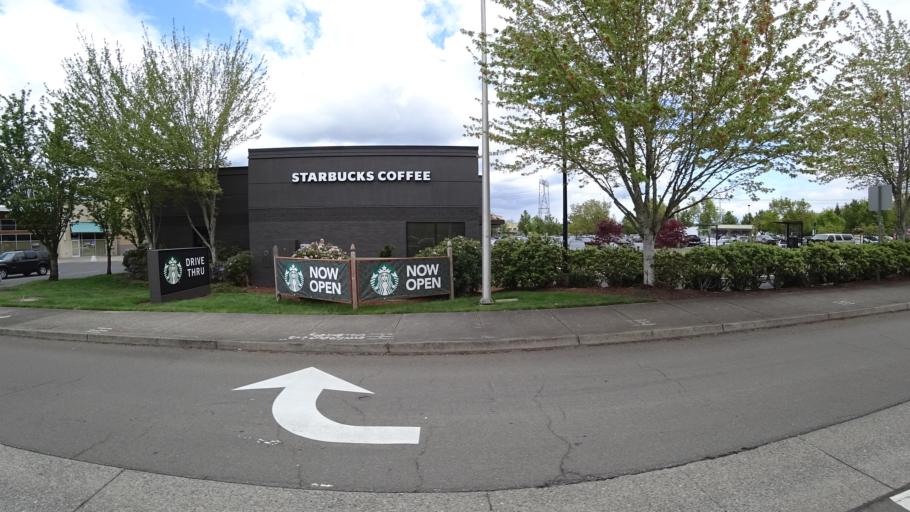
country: US
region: Oregon
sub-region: Washington County
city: Rockcreek
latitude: 45.5502
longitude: -122.9032
